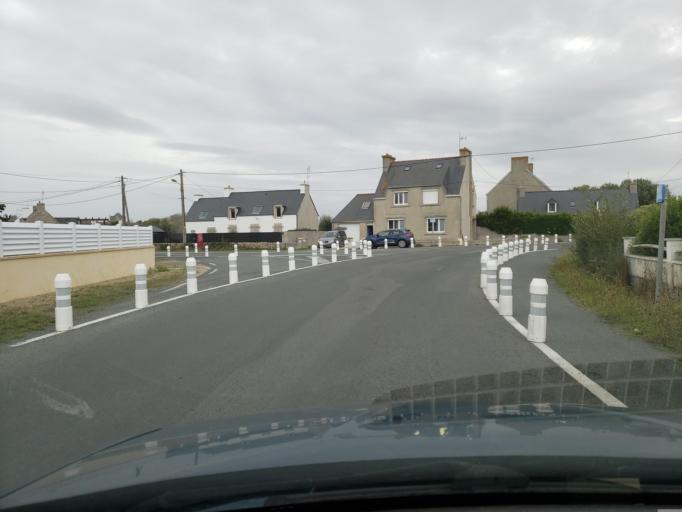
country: FR
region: Brittany
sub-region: Departement du Finistere
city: Plomeur
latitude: 47.8153
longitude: -4.3623
